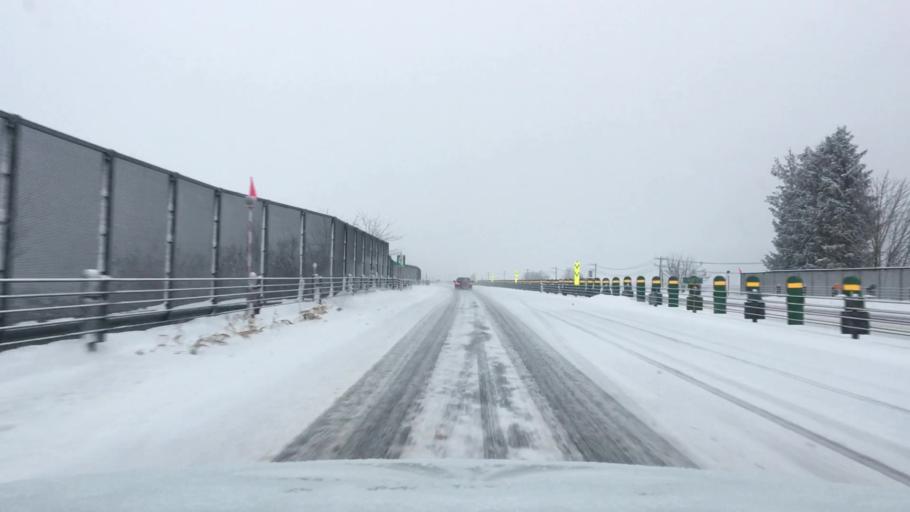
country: JP
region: Akita
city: Hanawa
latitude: 40.2778
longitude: 140.7614
